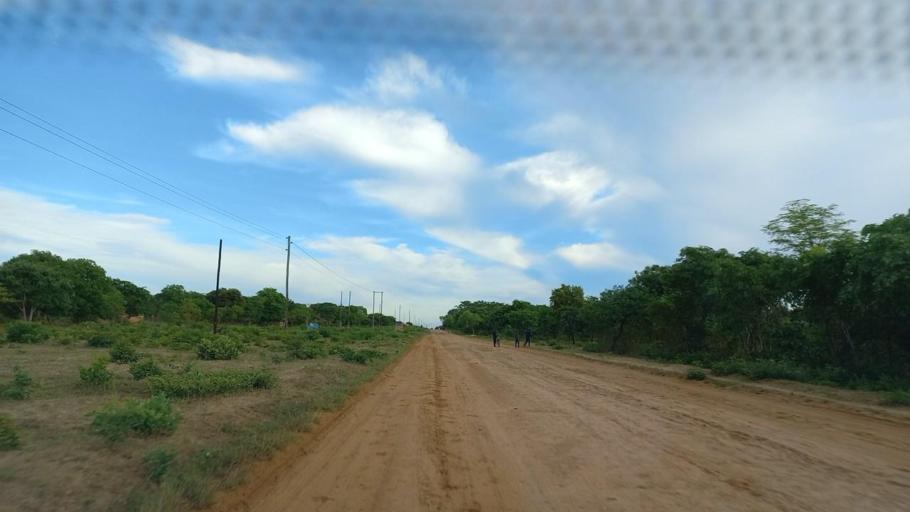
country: ZM
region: North-Western
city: Kabompo
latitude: -13.4232
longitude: 24.3240
